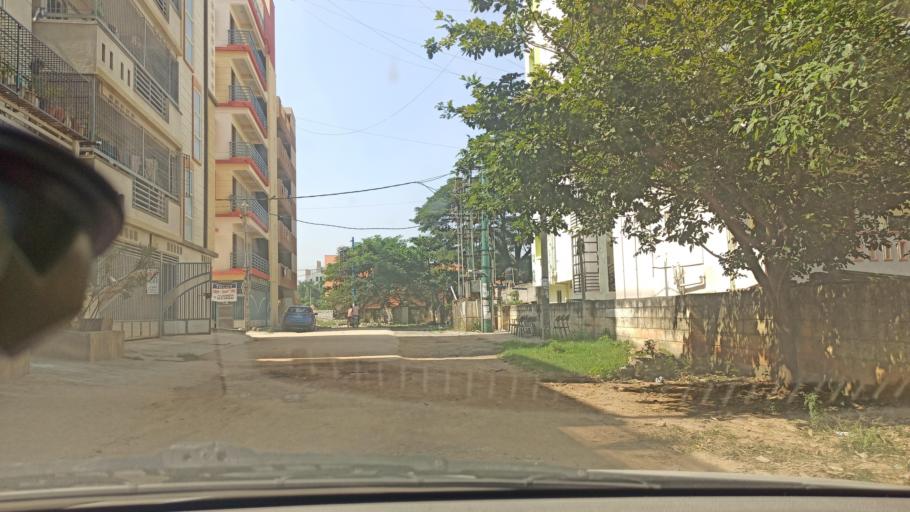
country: IN
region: Karnataka
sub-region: Bangalore Urban
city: Bangalore
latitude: 12.9464
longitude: 77.7026
